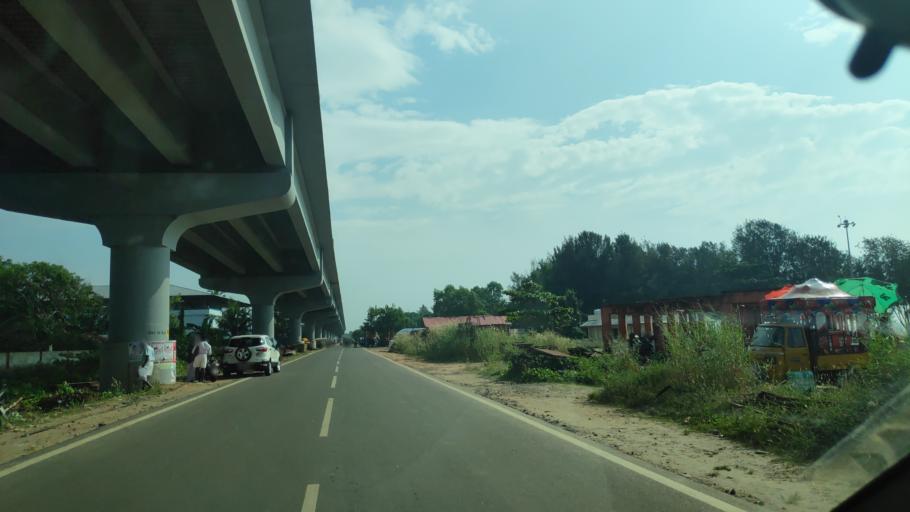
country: IN
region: Kerala
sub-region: Alappuzha
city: Alleppey
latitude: 9.4896
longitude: 76.3194
